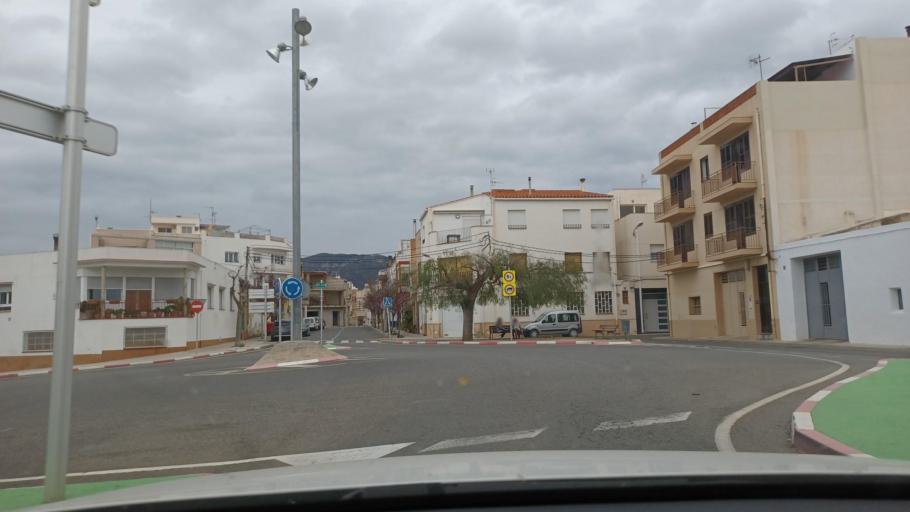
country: ES
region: Valencia
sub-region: Provincia de Castello
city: Rosell
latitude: 40.6330
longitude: 0.2848
